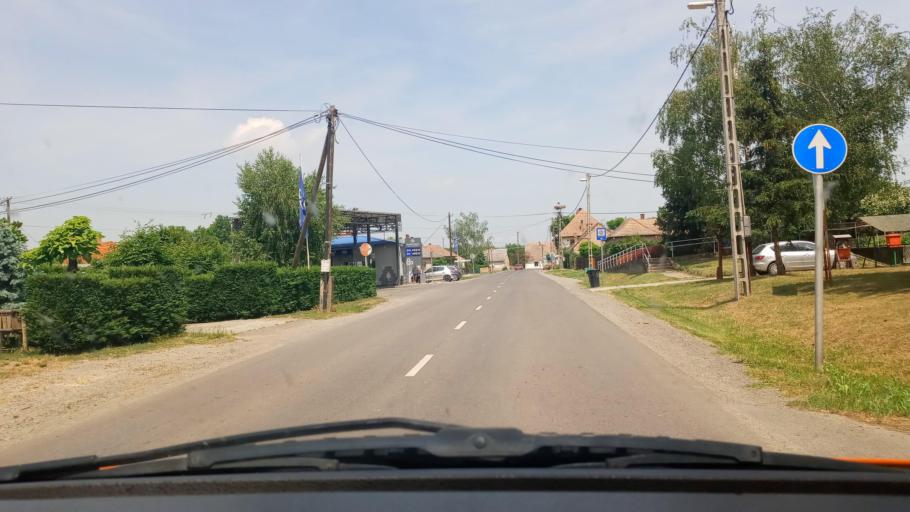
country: HU
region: Baranya
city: Szigetvar
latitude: 45.9732
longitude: 17.7214
